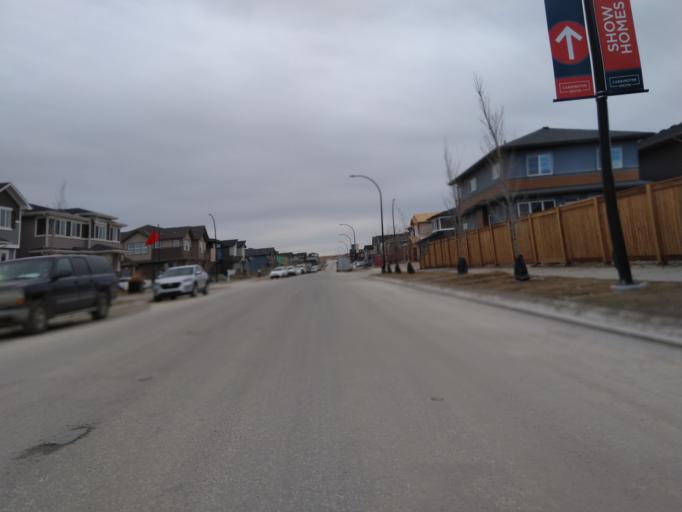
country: CA
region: Alberta
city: Calgary
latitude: 51.1787
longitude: -114.0880
